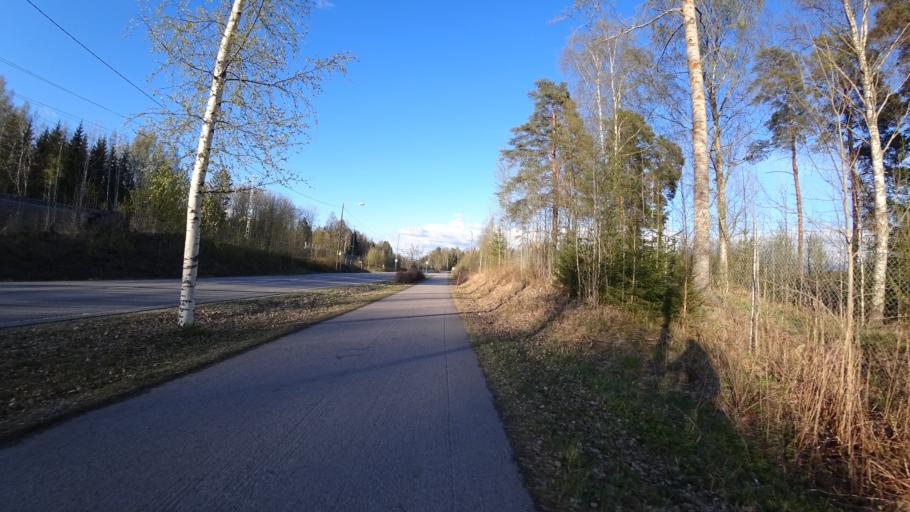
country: FI
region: Pirkanmaa
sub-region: Tampere
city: Nokia
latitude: 61.4941
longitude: 23.5625
